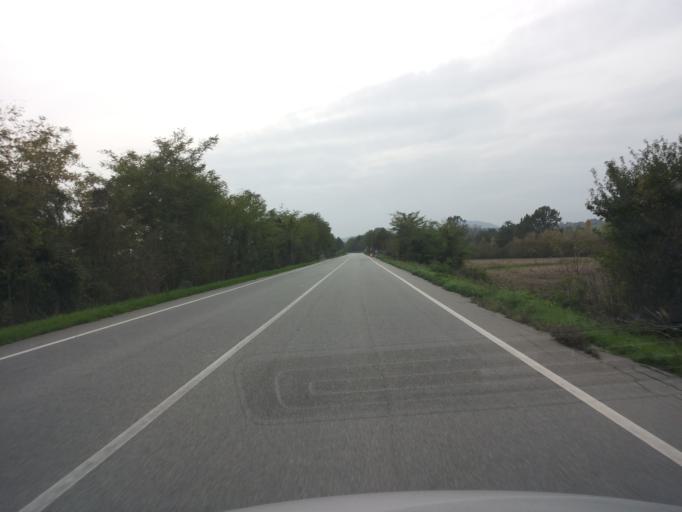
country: IT
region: Piedmont
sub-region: Provincia di Alessandria
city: Pontestura
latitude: 45.1342
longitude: 8.3414
